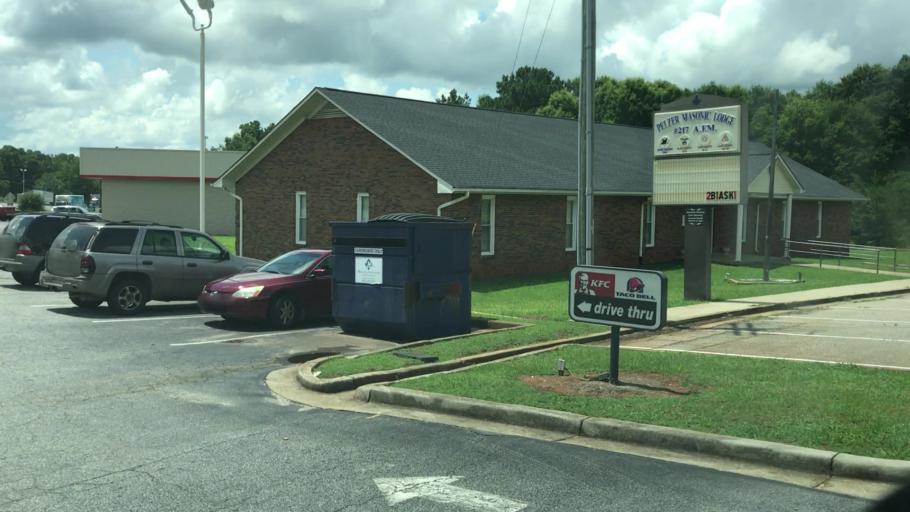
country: US
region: South Carolina
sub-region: Anderson County
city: Williamston
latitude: 34.6428
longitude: -82.4669
